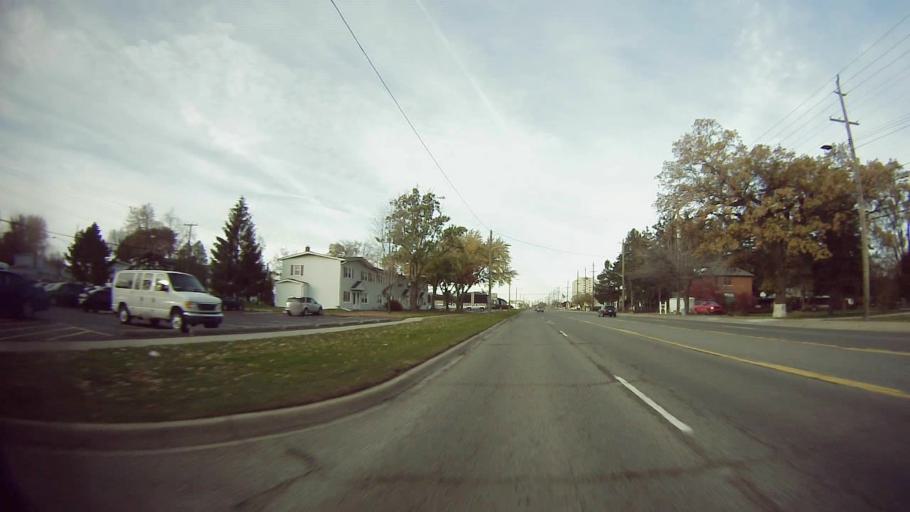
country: US
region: Michigan
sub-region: Macomb County
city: Warren
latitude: 42.4775
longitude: -83.0219
